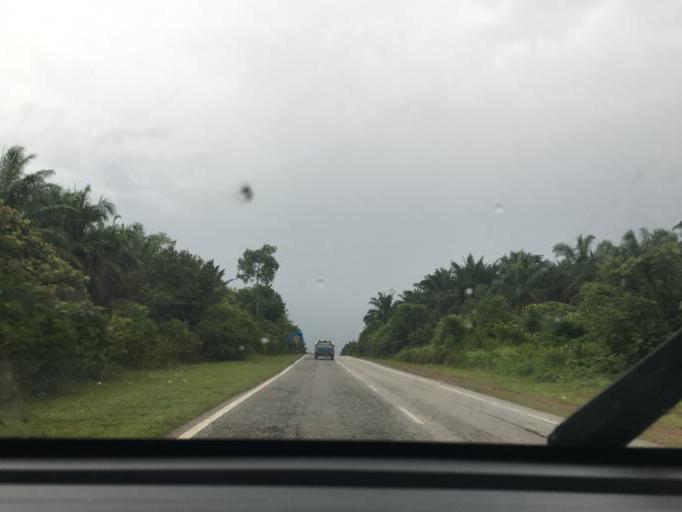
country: MY
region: Kedah
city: Sungai Petani
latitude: 5.6271
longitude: 100.6344
